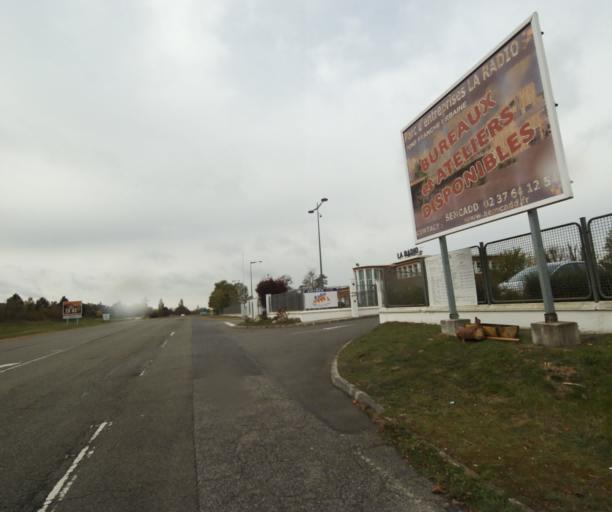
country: FR
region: Centre
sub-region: Departement d'Eure-et-Loir
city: Luray
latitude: 48.7473
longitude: 1.4001
